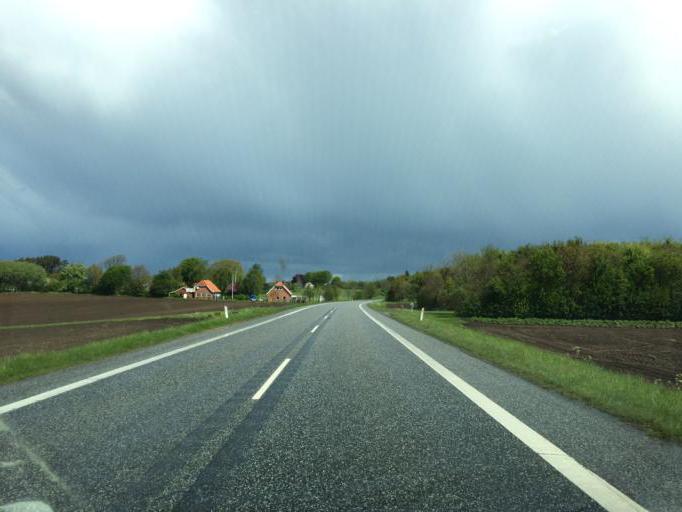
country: DK
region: Central Jutland
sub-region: Skive Kommune
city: Hojslev
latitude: 56.5688
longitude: 9.1174
